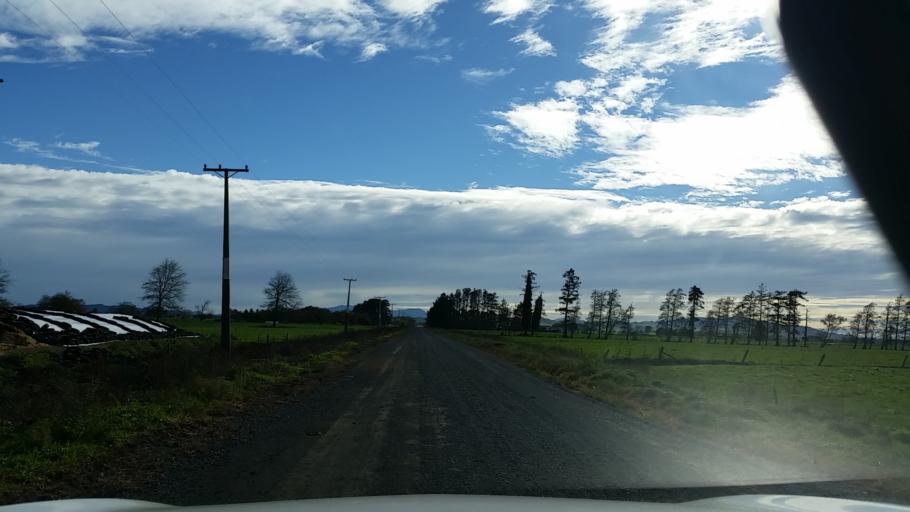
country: NZ
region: Waikato
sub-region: Hamilton City
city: Hamilton
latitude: -37.6630
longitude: 175.4380
